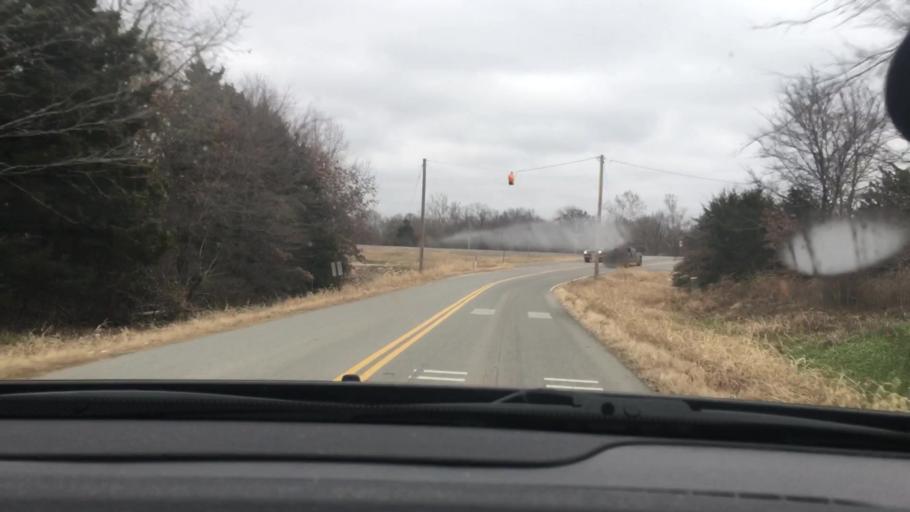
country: US
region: Oklahoma
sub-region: Atoka County
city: Atoka
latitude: 34.3439
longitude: -96.0754
